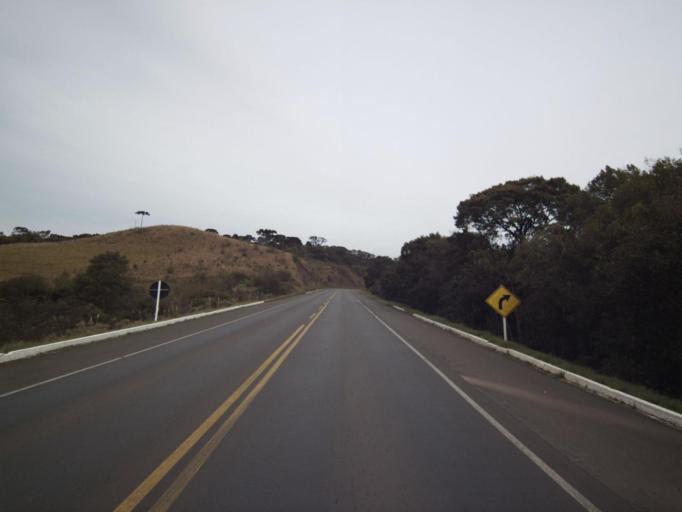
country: BR
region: Parana
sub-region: Palmas
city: Palmas
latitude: -26.6440
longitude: -51.5134
